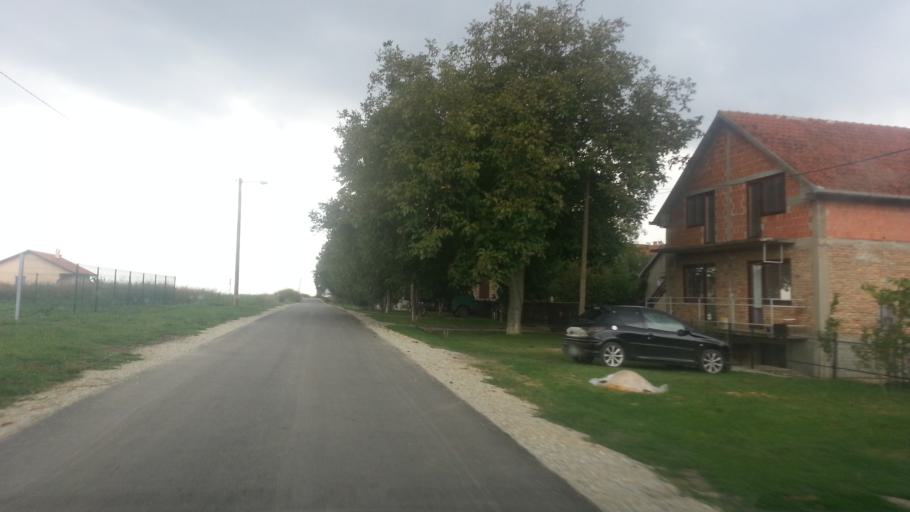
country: RS
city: Novi Banovci
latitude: 44.9605
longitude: 20.2740
